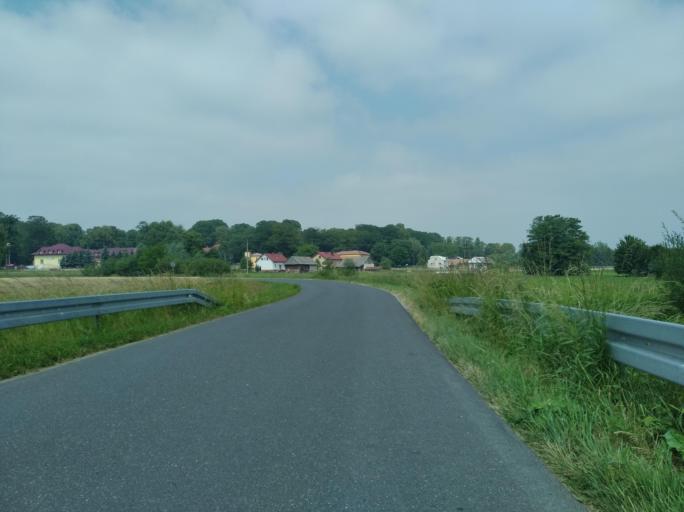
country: PL
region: Subcarpathian Voivodeship
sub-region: Powiat brzozowski
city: Haczow
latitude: 49.6304
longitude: 21.9226
